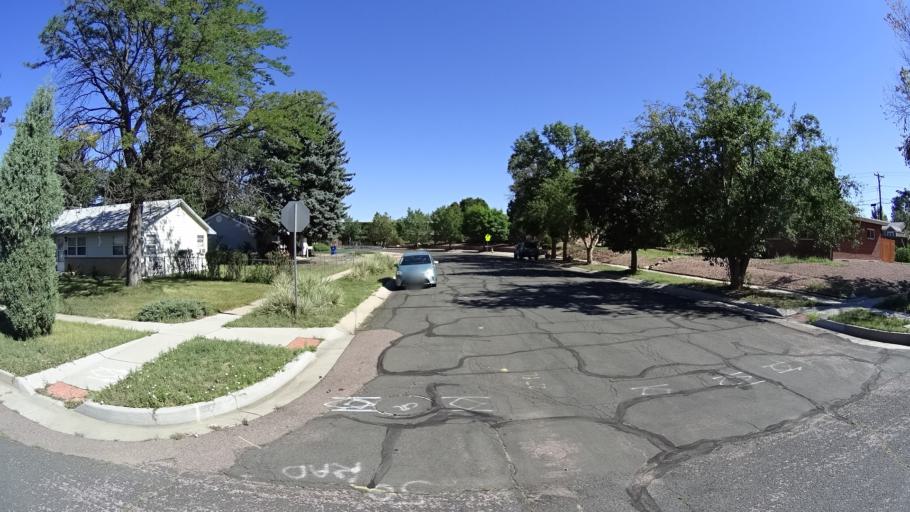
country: US
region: Colorado
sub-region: El Paso County
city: Colorado Springs
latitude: 38.8678
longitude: -104.7974
